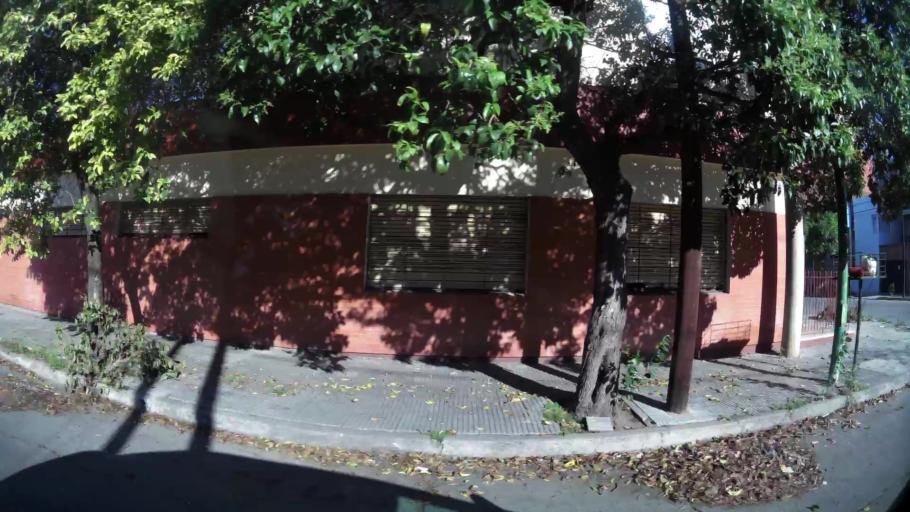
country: AR
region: Cordoba
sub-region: Departamento de Capital
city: Cordoba
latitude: -31.3867
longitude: -64.1767
